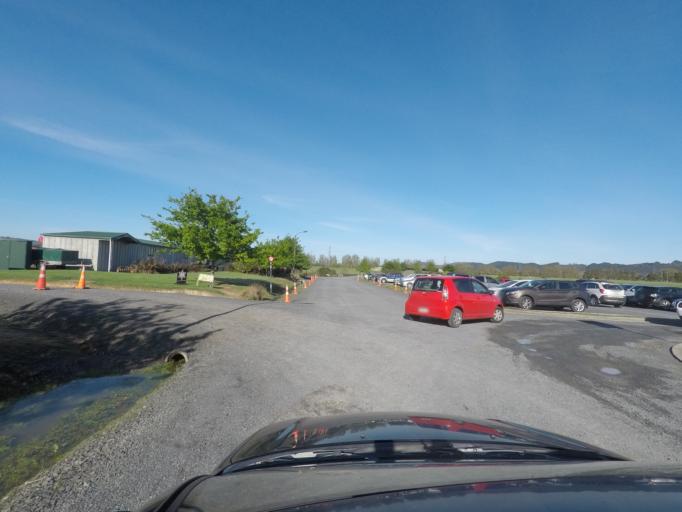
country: NZ
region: Auckland
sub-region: Auckland
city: Red Hill
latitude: -37.0044
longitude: 175.0423
